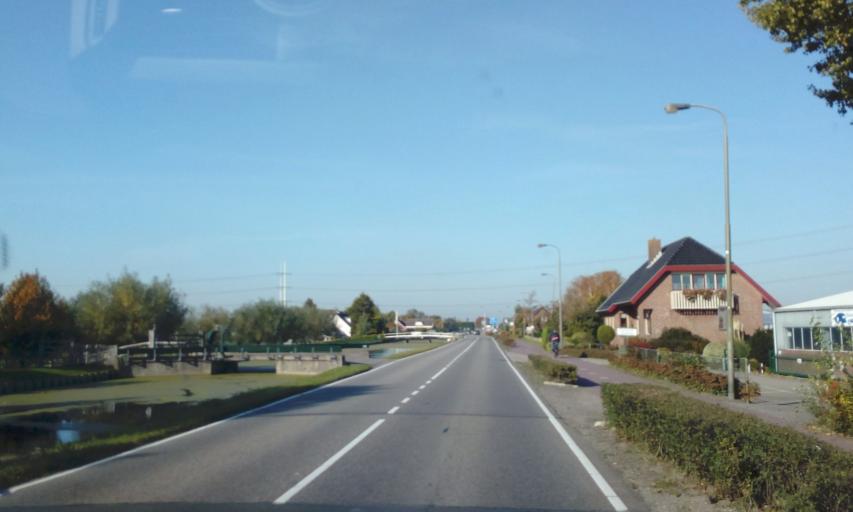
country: NL
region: South Holland
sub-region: Gemeente Zoetermeer
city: Zoetermeer
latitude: 52.0281
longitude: 4.4798
